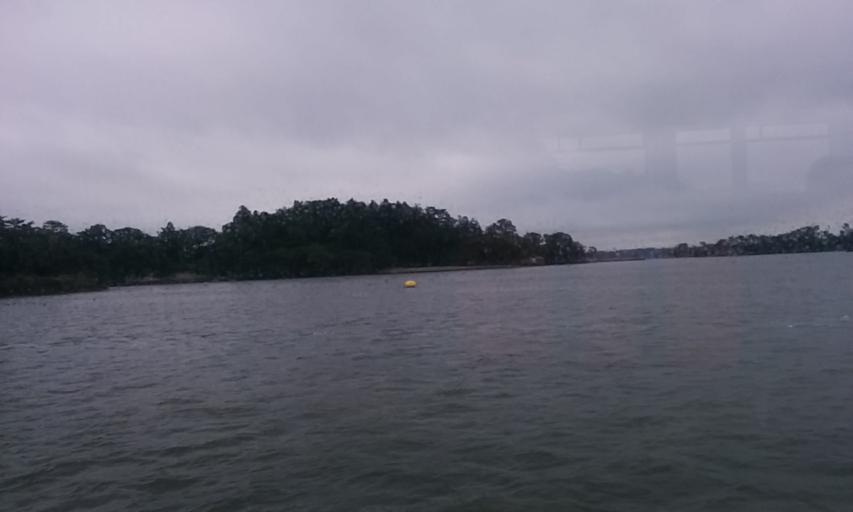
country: JP
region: Miyagi
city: Matsushima
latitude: 38.3633
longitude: 141.0676
